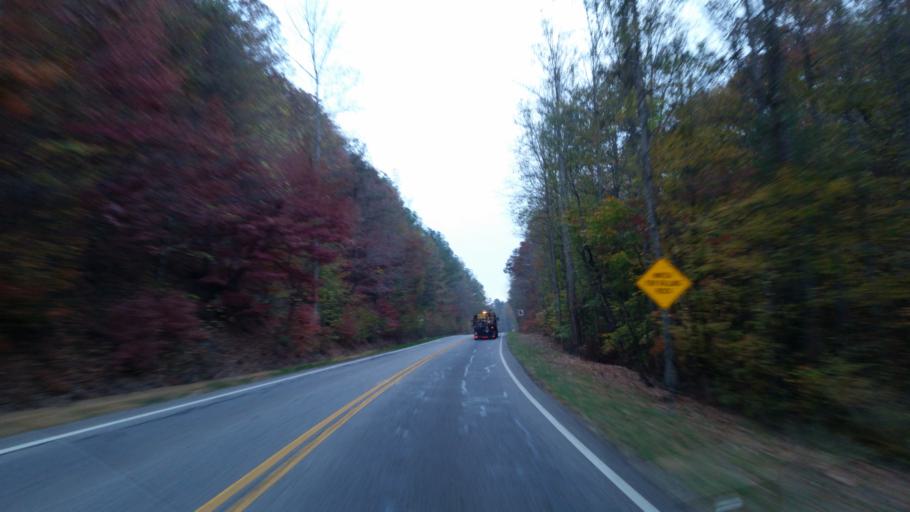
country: US
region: Georgia
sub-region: Gilmer County
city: Ellijay
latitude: 34.5811
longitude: -84.6506
